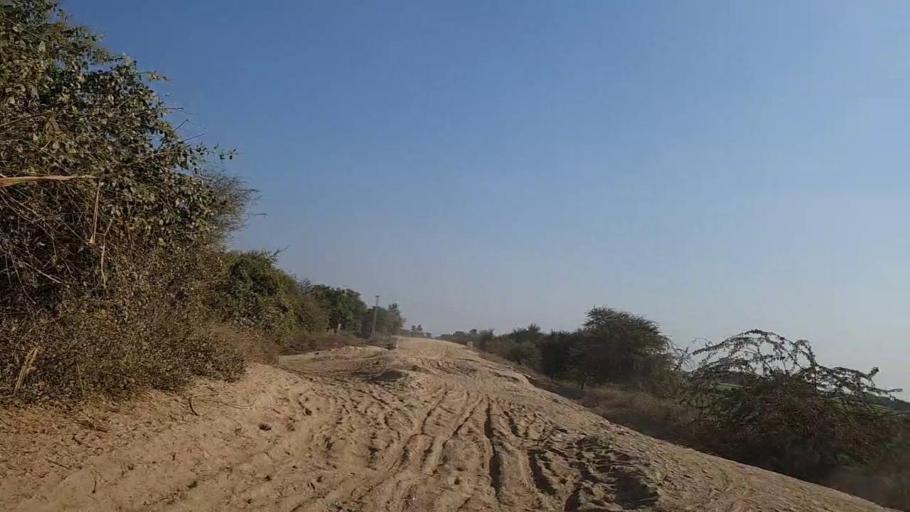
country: PK
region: Sindh
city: Sakrand
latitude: 26.0144
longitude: 68.3161
